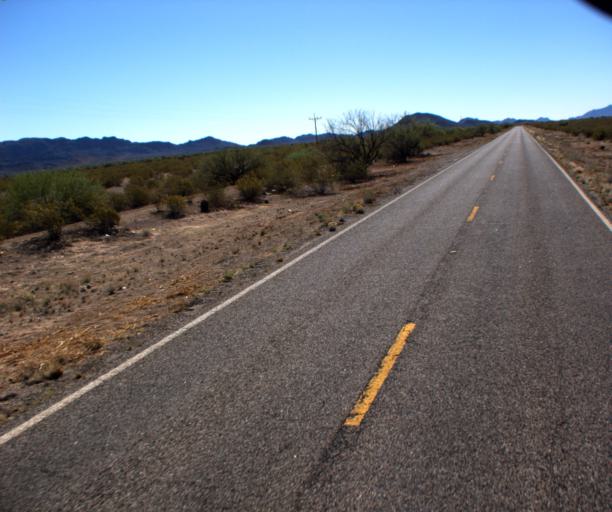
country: US
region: Arizona
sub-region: Pima County
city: Ajo
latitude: 32.3142
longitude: -112.7658
